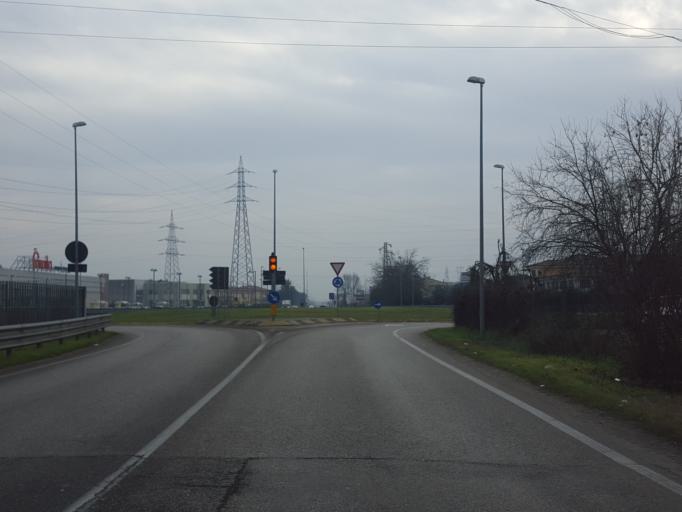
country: IT
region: Veneto
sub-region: Provincia di Verona
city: San Bonifacio
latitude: 45.3875
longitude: 11.2810
